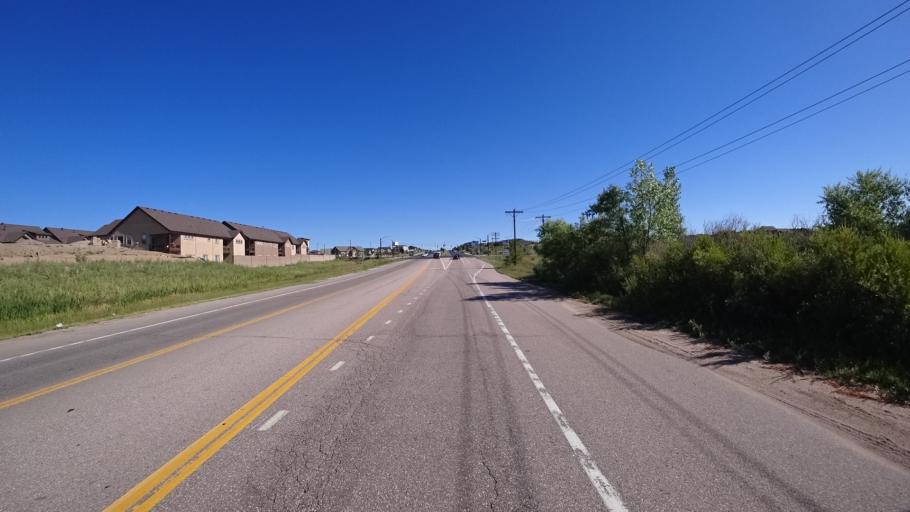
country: US
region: Colorado
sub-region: El Paso County
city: Cimarron Hills
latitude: 38.9249
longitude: -104.6828
